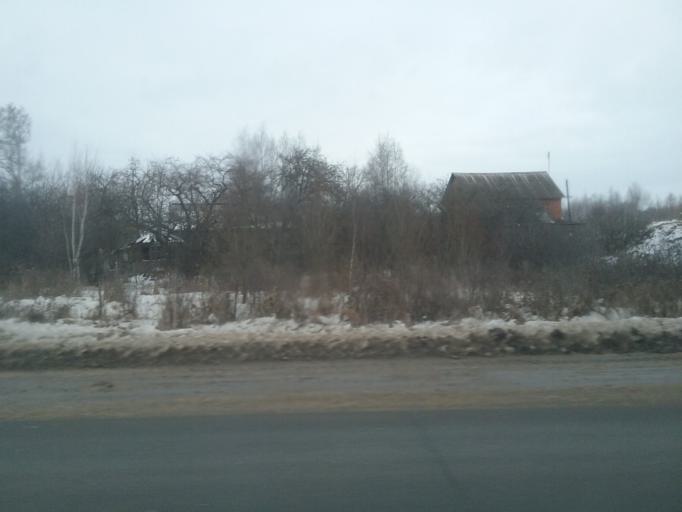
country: RU
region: Tula
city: Bolokhovo
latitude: 54.0544
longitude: 37.8089
